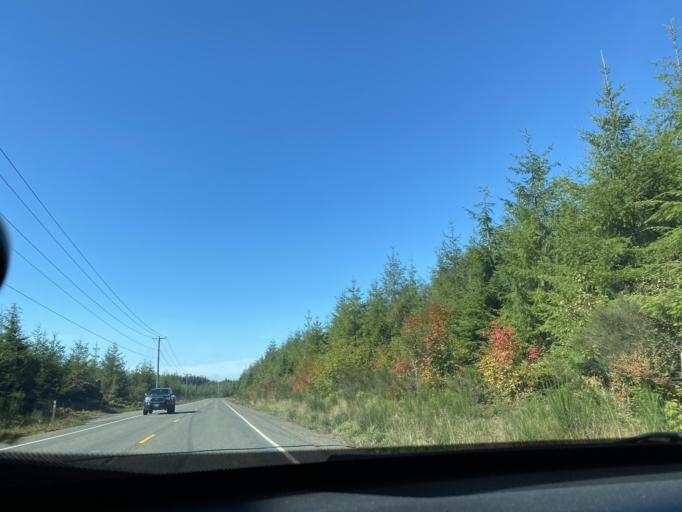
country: US
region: Washington
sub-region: Clallam County
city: Forks
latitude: 47.9634
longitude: -124.4217
